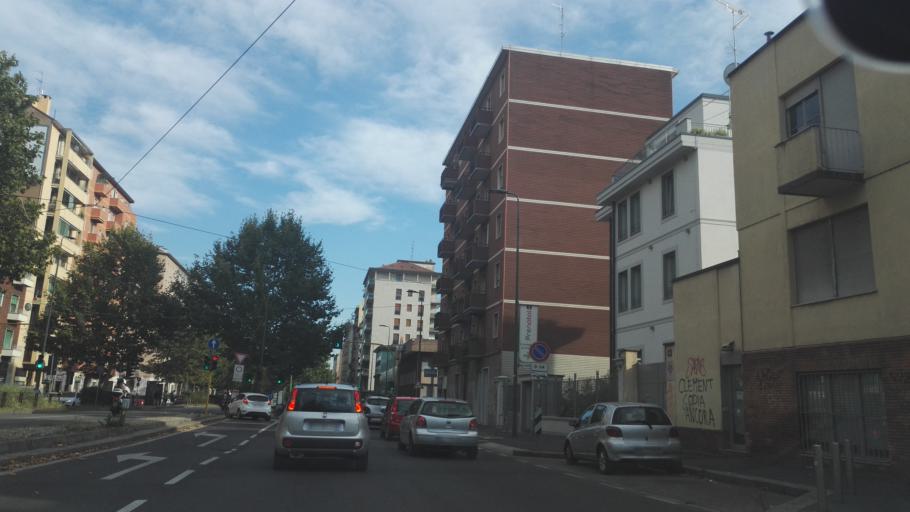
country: IT
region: Lombardy
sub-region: Citta metropolitana di Milano
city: Milano
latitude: 45.4581
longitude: 9.1508
